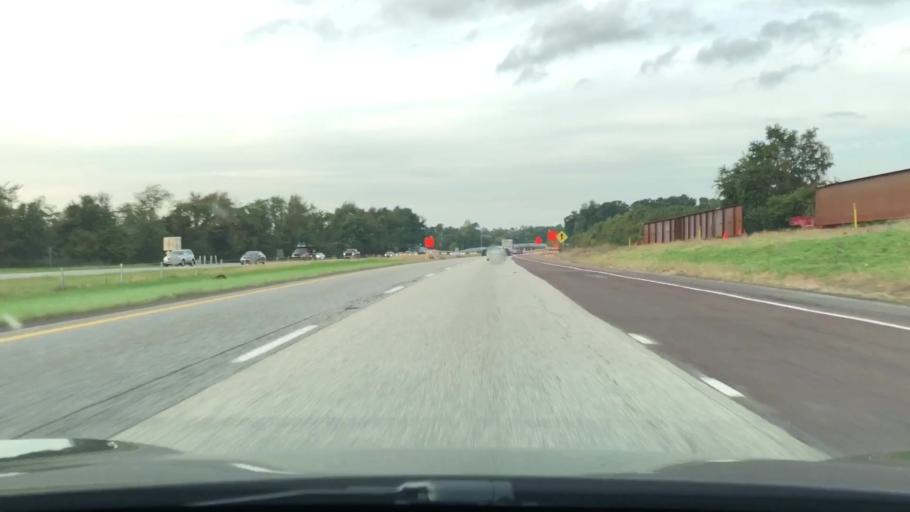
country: US
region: Pennsylvania
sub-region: Bucks County
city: Woodside
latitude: 40.2355
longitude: -74.8818
